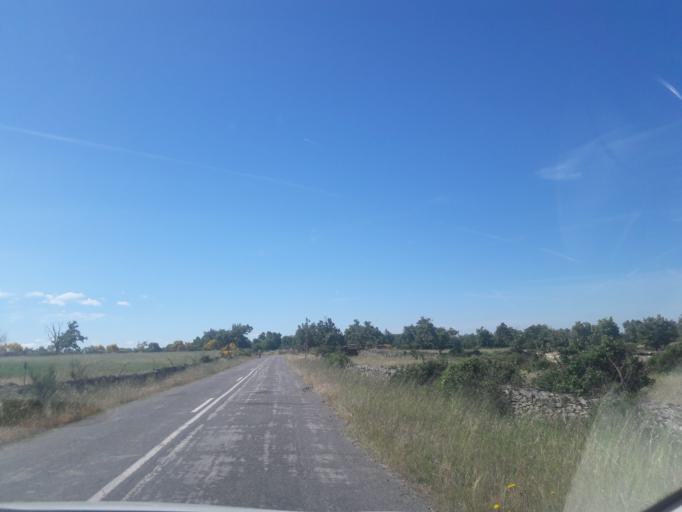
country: ES
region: Castille and Leon
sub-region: Provincia de Salamanca
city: Lumbrales
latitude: 40.9531
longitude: -6.7191
